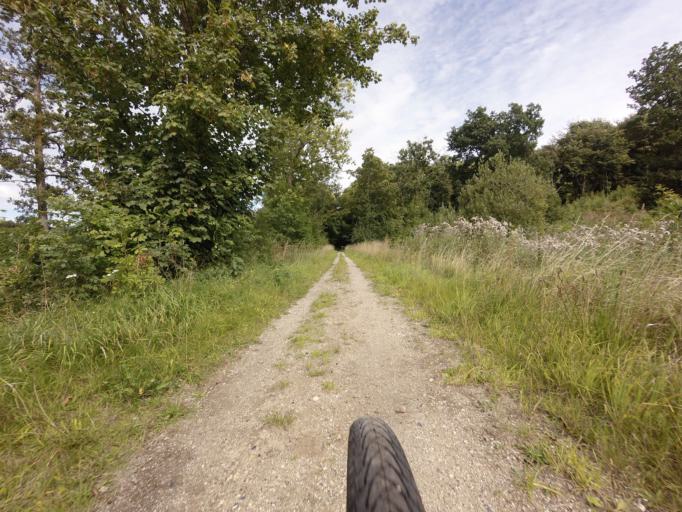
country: DK
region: Central Jutland
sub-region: Syddjurs Kommune
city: Ryomgard
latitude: 56.3820
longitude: 10.5309
